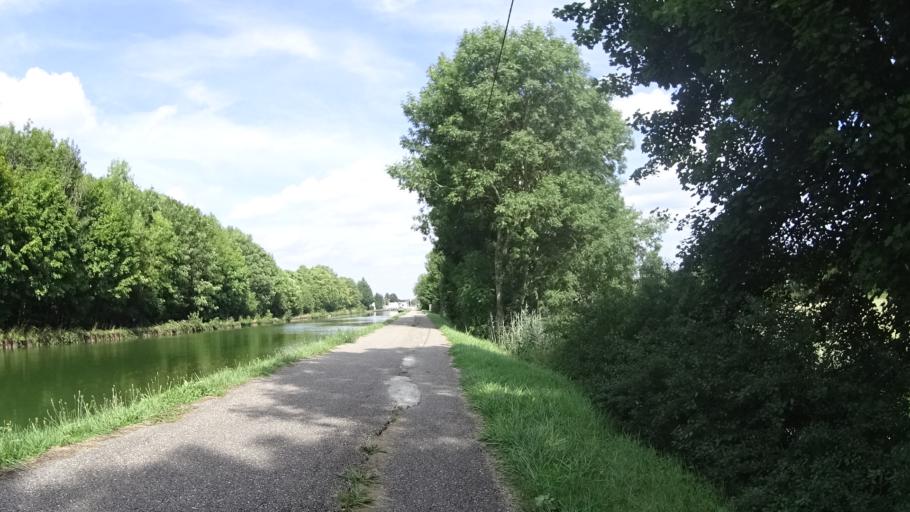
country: FR
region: Lorraine
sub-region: Departement de Meurthe-et-Moselle
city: Toul
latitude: 48.6772
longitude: 5.8777
